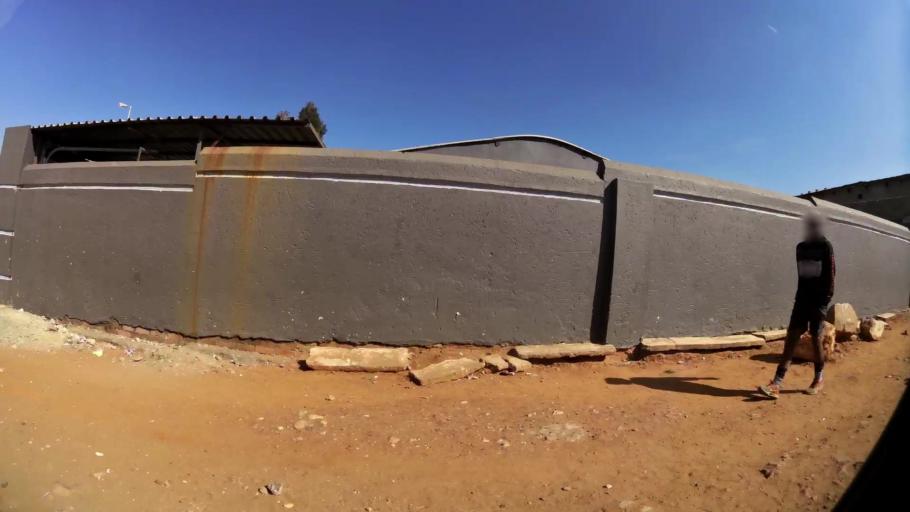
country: ZA
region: Gauteng
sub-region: City of Johannesburg Metropolitan Municipality
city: Soweto
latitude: -26.2324
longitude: 27.8839
